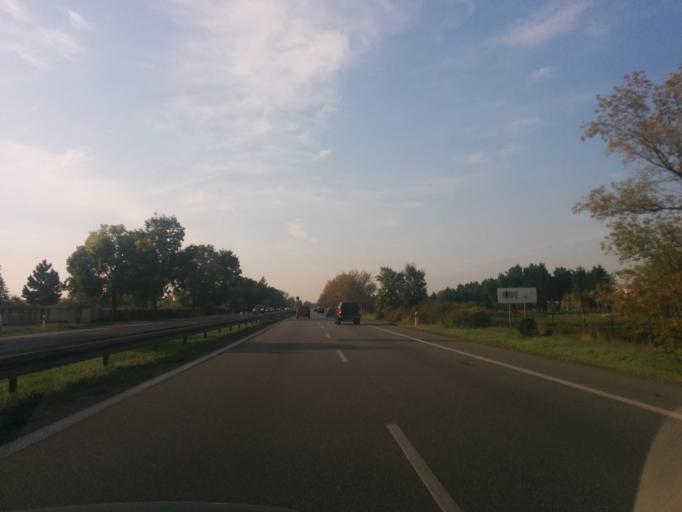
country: PL
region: Masovian Voivodeship
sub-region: Powiat piaseczynski
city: Tarczyn
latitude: 52.0346
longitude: 20.8595
